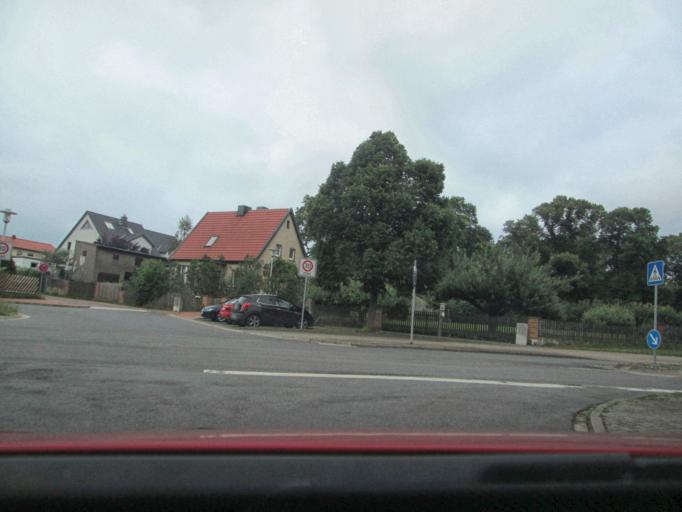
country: DE
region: Lower Saxony
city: Weyhausen
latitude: 52.3969
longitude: 10.7007
